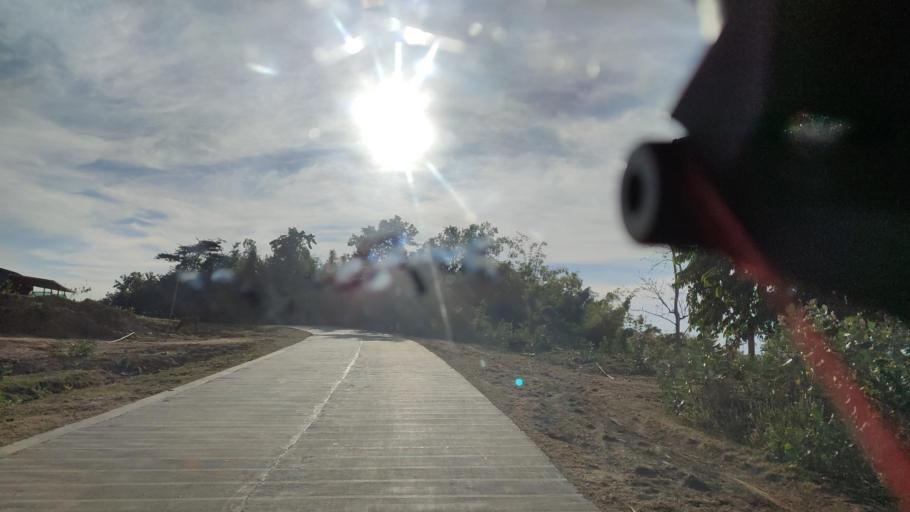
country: MM
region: Magway
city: Taungdwingyi
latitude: 20.0245
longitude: 95.8205
